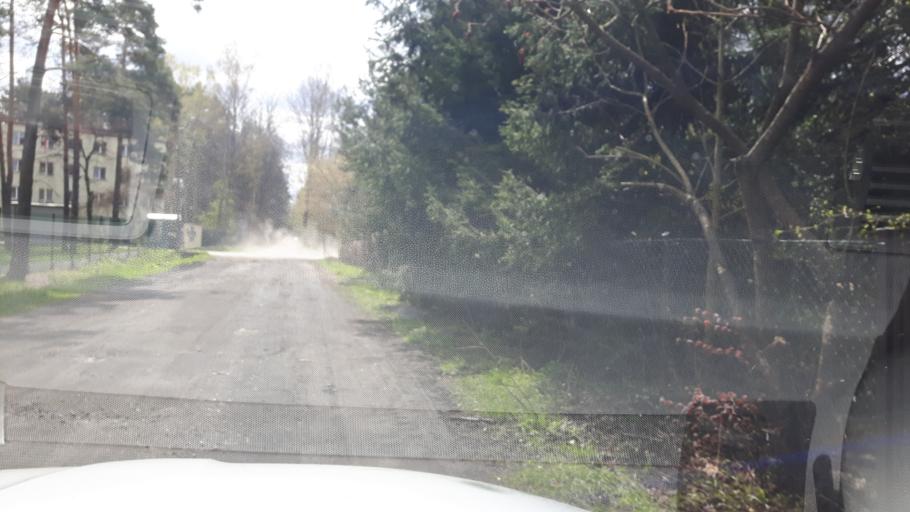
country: PL
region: Masovian Voivodeship
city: Zielonka
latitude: 52.2979
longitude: 21.1672
